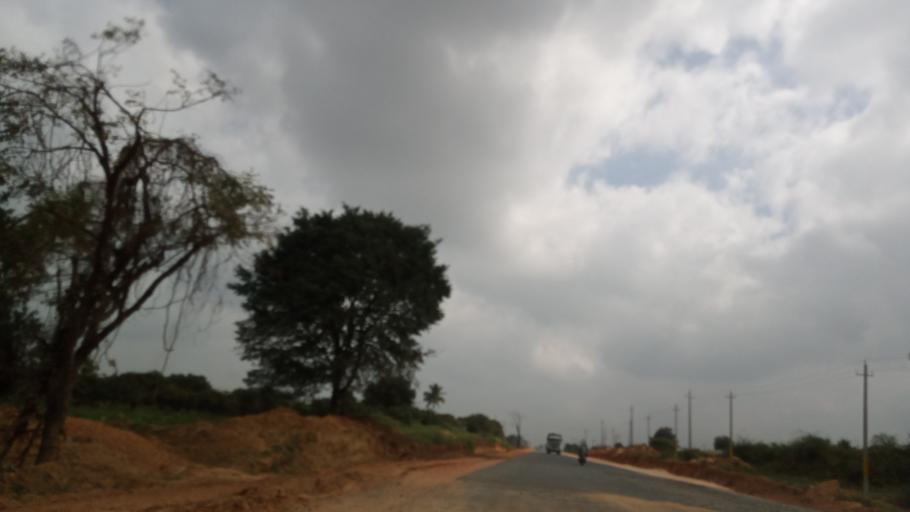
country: IN
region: Karnataka
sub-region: Kolar
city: Srinivaspur
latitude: 13.4457
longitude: 78.2367
